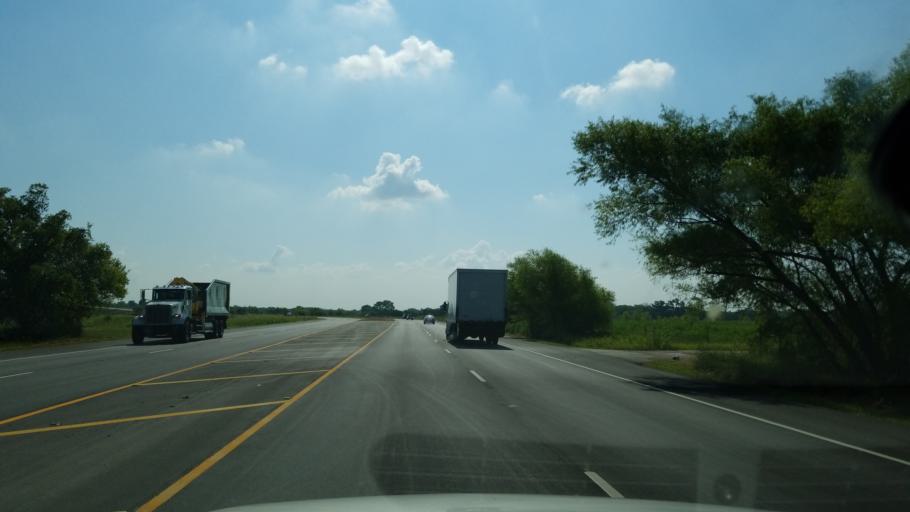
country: US
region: Texas
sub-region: Tarrant County
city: Hurst
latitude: 32.8013
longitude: -97.1487
